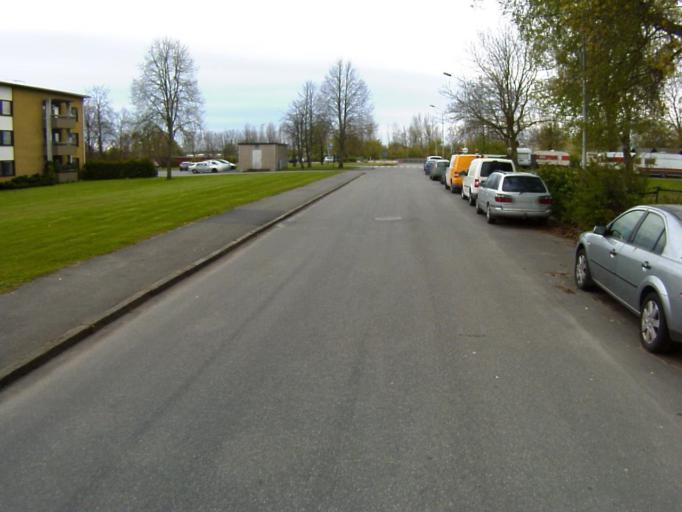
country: SE
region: Skane
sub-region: Kristianstads Kommun
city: Kristianstad
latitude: 56.0201
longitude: 14.1280
